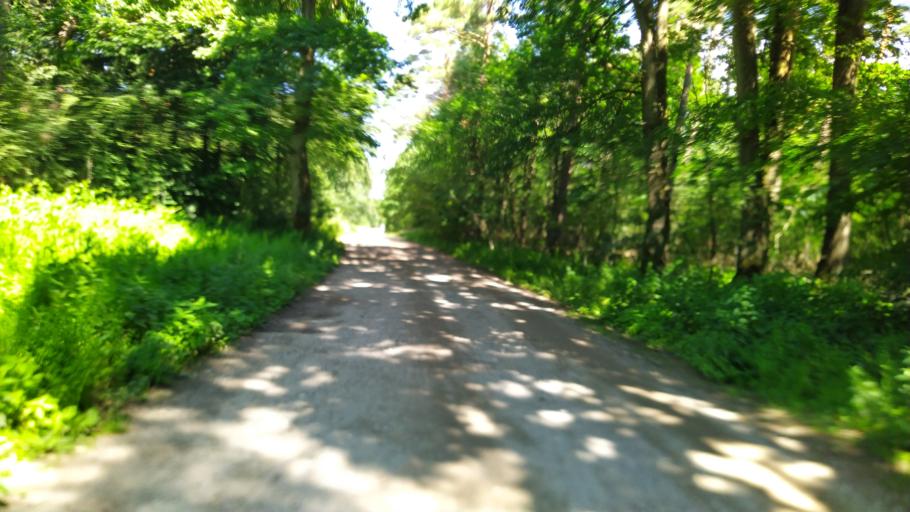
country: DE
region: Lower Saxony
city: Deinste
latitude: 53.5020
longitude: 9.4416
